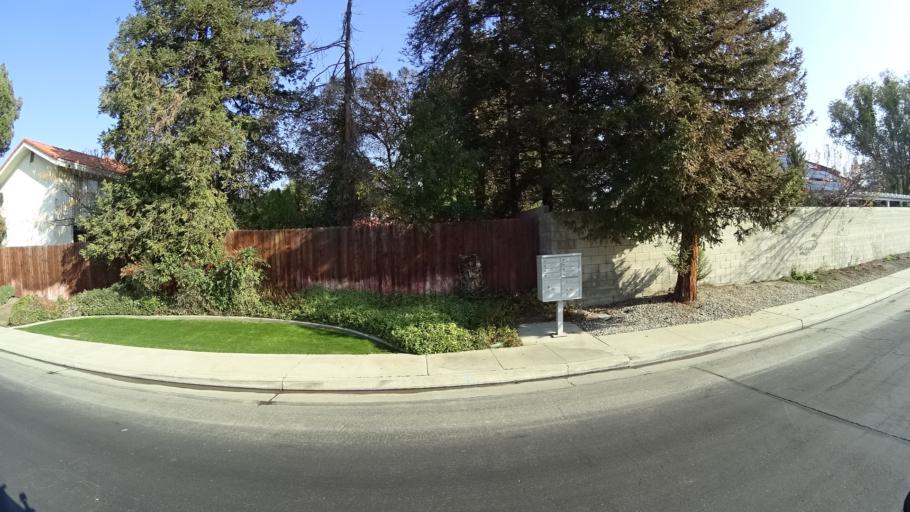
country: US
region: California
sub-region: Kern County
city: Greenacres
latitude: 35.3388
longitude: -119.1103
